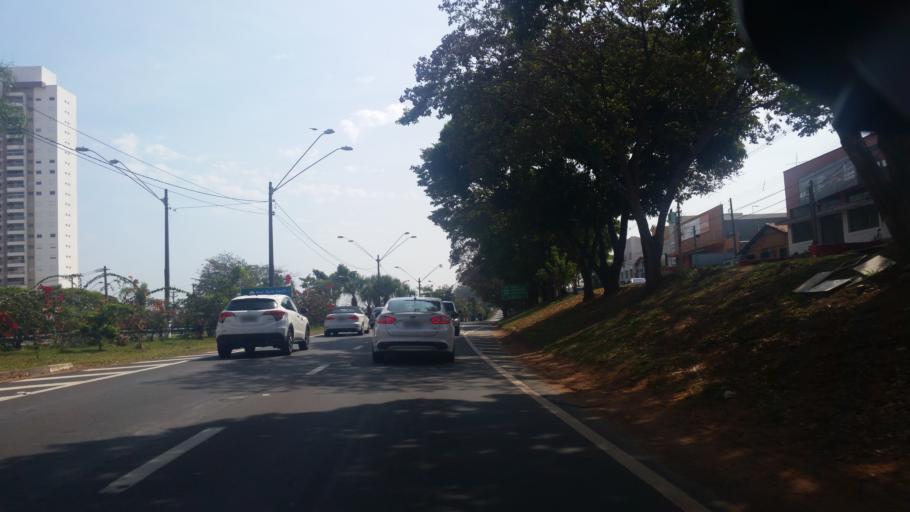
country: BR
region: Sao Paulo
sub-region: Campinas
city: Campinas
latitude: -22.8548
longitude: -47.0439
